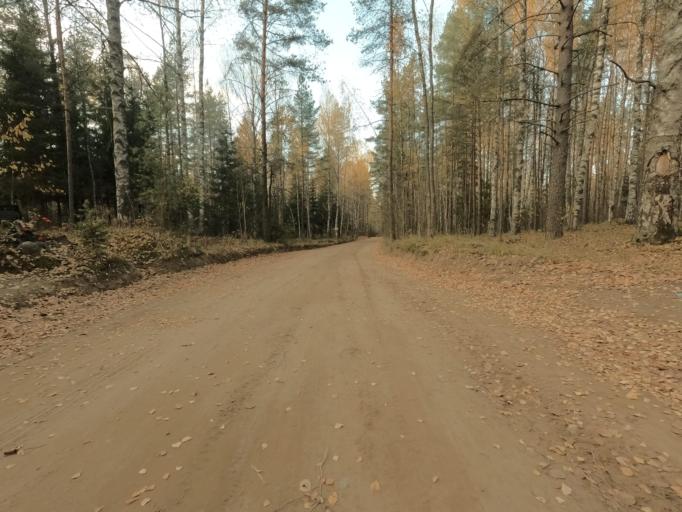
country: RU
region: Leningrad
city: Priladozhskiy
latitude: 59.7407
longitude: 31.3146
